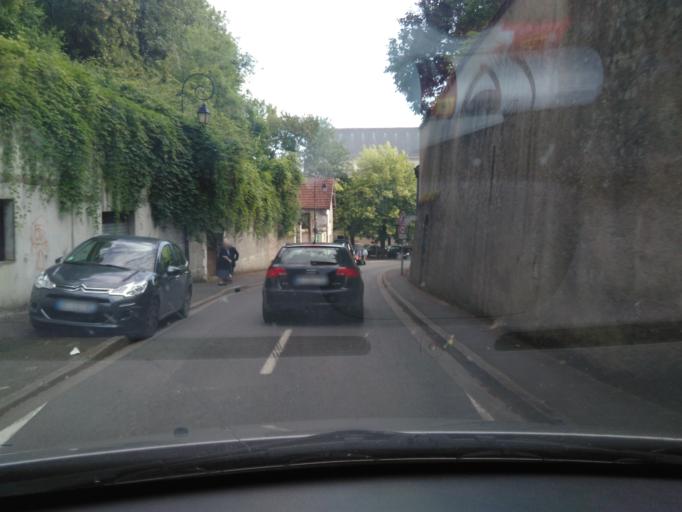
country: FR
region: Centre
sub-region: Departement d'Indre-et-Loire
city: Amboise
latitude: 47.4089
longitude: 0.9779
